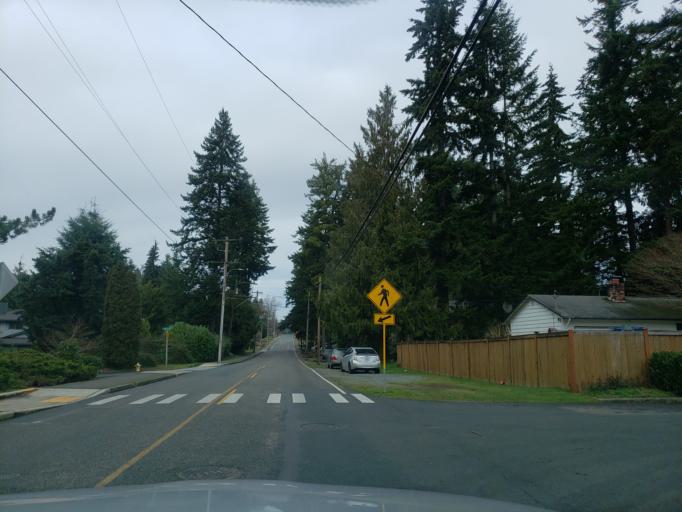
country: US
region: Washington
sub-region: Snohomish County
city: Lynnwood
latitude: 47.8225
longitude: -122.3414
